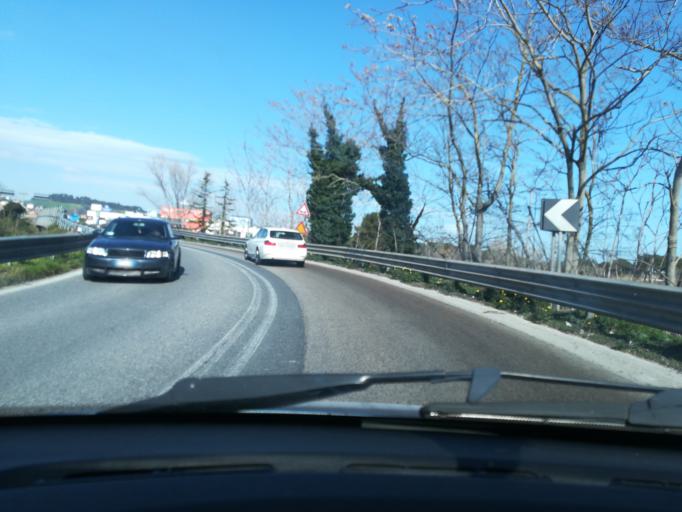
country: IT
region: The Marches
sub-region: Provincia di Macerata
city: Santa Maria Apparente
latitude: 43.2880
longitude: 13.7099
